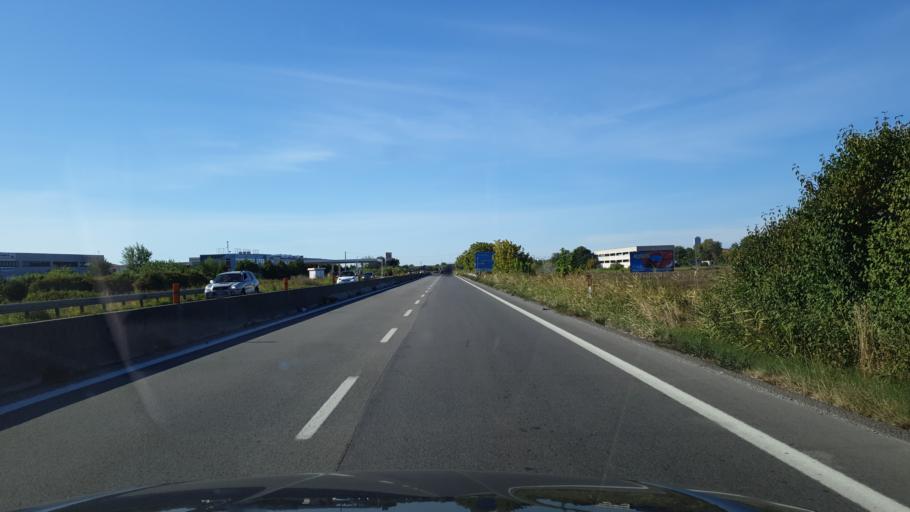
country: IT
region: Emilia-Romagna
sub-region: Forli-Cesena
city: Gatteo a Mare
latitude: 44.1735
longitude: 12.4184
